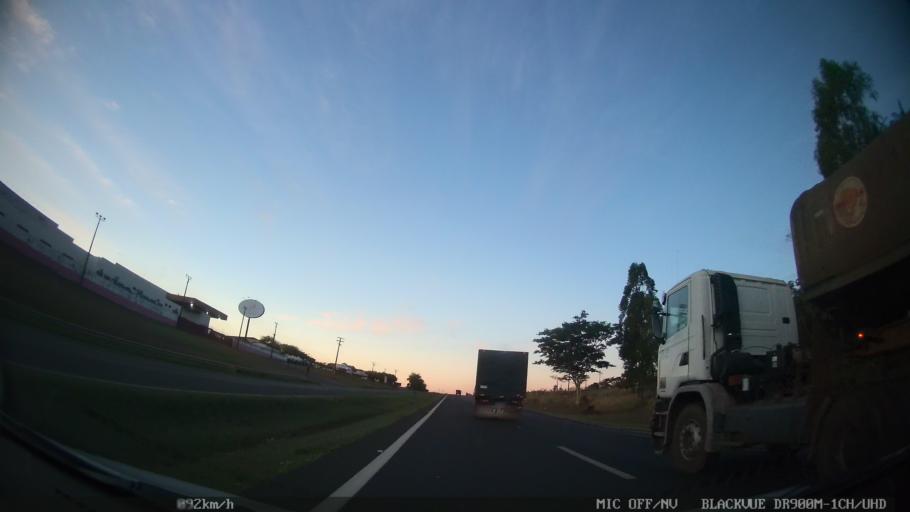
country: BR
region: Sao Paulo
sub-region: Catanduva
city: Catanduva
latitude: -21.1113
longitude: -48.9682
